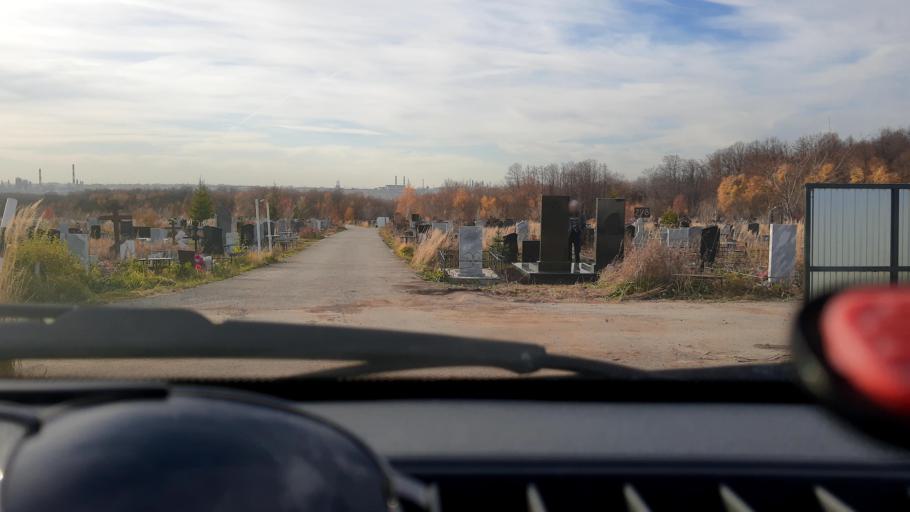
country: RU
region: Bashkortostan
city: Ufa
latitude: 54.8625
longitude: 56.1626
